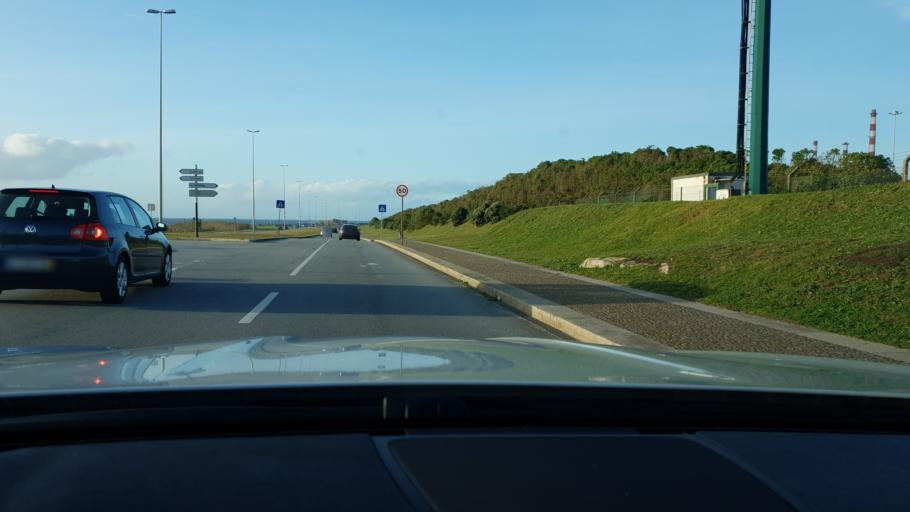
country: PT
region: Porto
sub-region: Matosinhos
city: Leca da Palmeira
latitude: 41.2024
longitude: -8.7118
